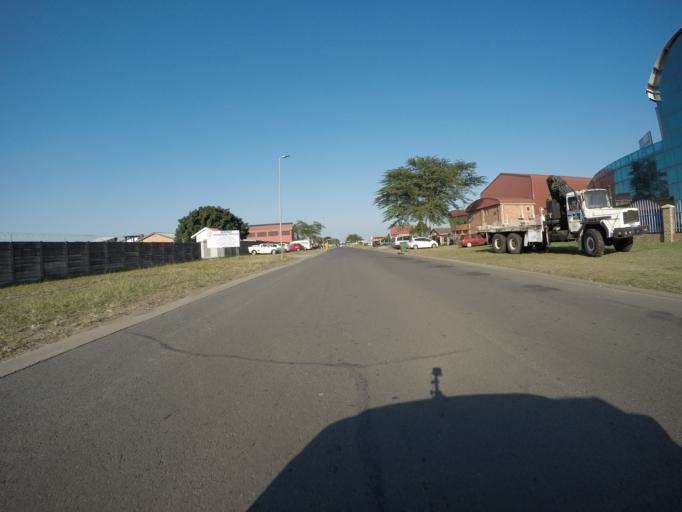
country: ZA
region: KwaZulu-Natal
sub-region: uThungulu District Municipality
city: Richards Bay
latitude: -28.7376
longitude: 32.0394
